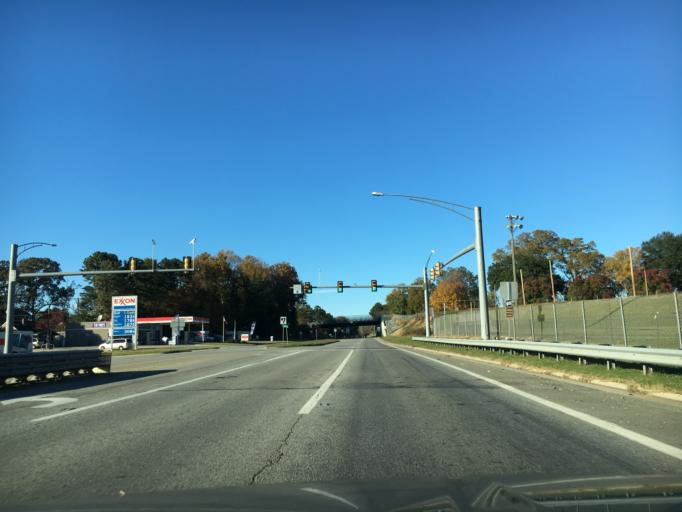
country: US
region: Virginia
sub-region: Halifax County
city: South Boston
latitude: 36.6970
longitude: -78.8880
